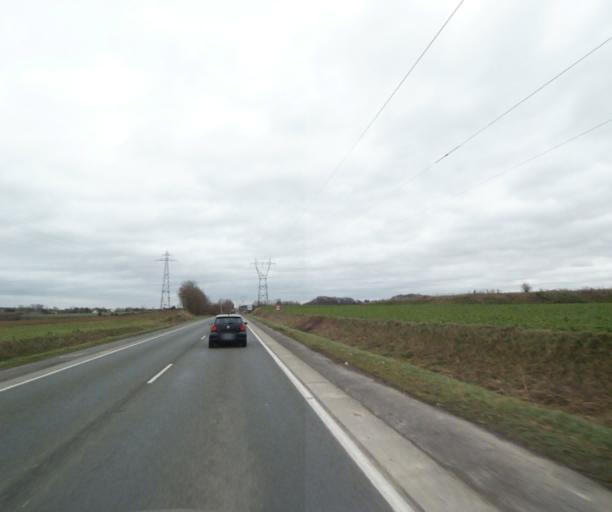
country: FR
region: Nord-Pas-de-Calais
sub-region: Departement du Nord
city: Marly
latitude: 50.3518
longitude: 3.5581
